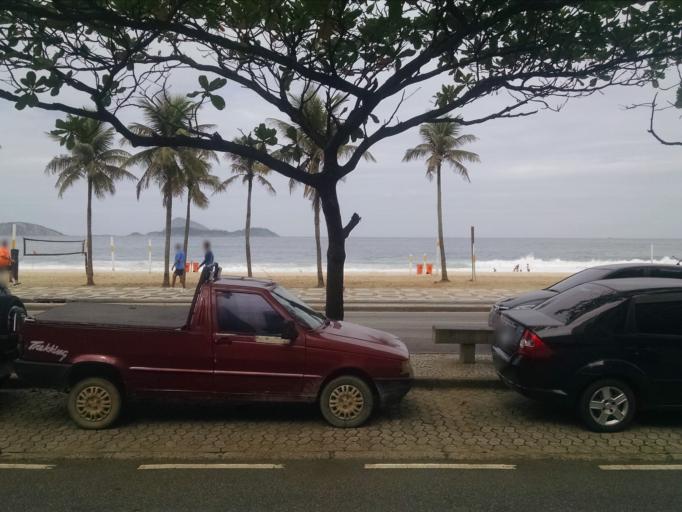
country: BR
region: Rio de Janeiro
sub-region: Rio De Janeiro
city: Rio de Janeiro
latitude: -22.9863
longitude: -43.2090
